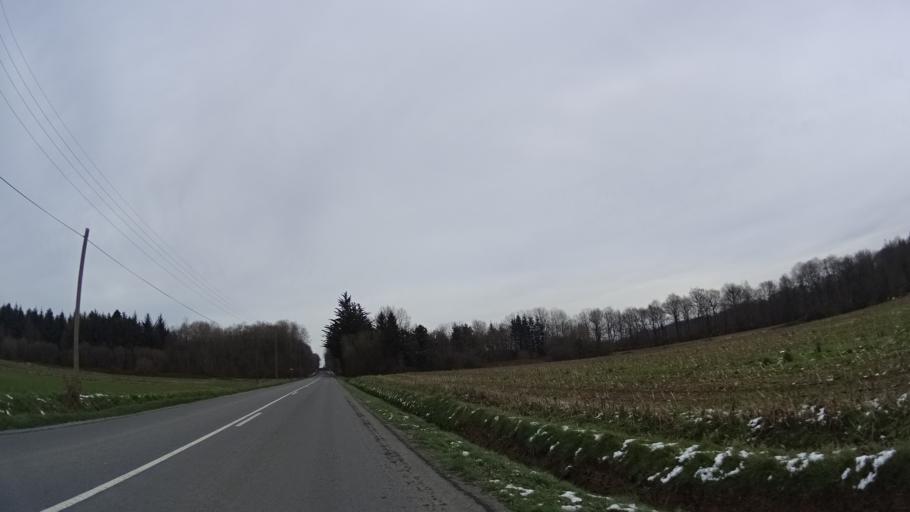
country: FR
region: Brittany
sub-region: Departement d'Ille-et-Vilaine
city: Montauban-de-Bretagne
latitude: 48.2186
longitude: -2.0286
